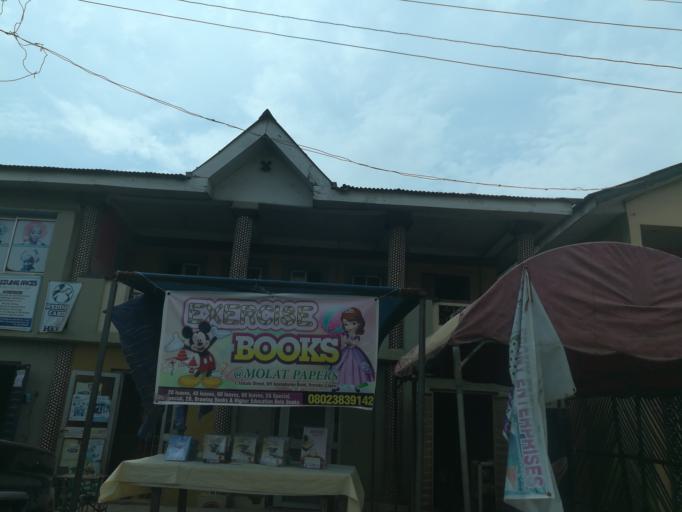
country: NG
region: Lagos
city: Ikorodu
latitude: 6.6152
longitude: 3.5027
